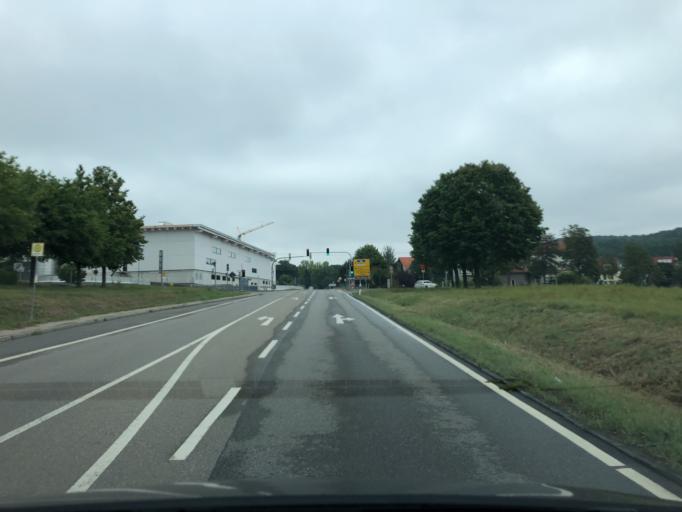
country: DE
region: Baden-Wuerttemberg
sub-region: Regierungsbezirk Stuttgart
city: Ehningen
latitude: 48.6604
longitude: 8.9523
